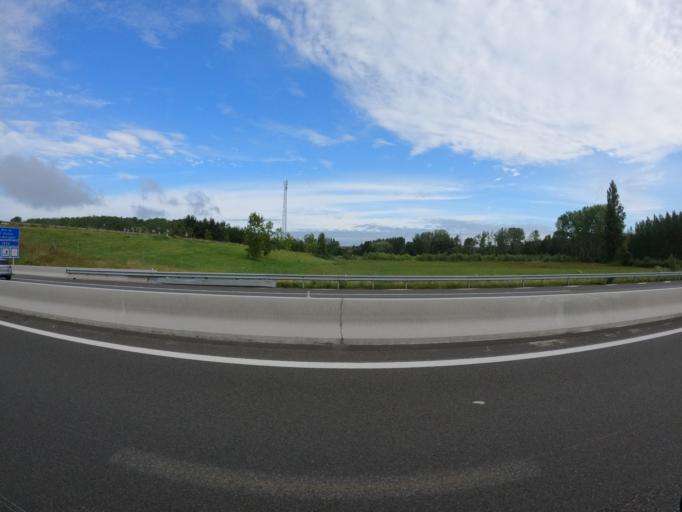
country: FR
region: Centre
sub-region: Departement d'Indre-et-Loire
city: Restigne
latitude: 47.2763
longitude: 0.2712
